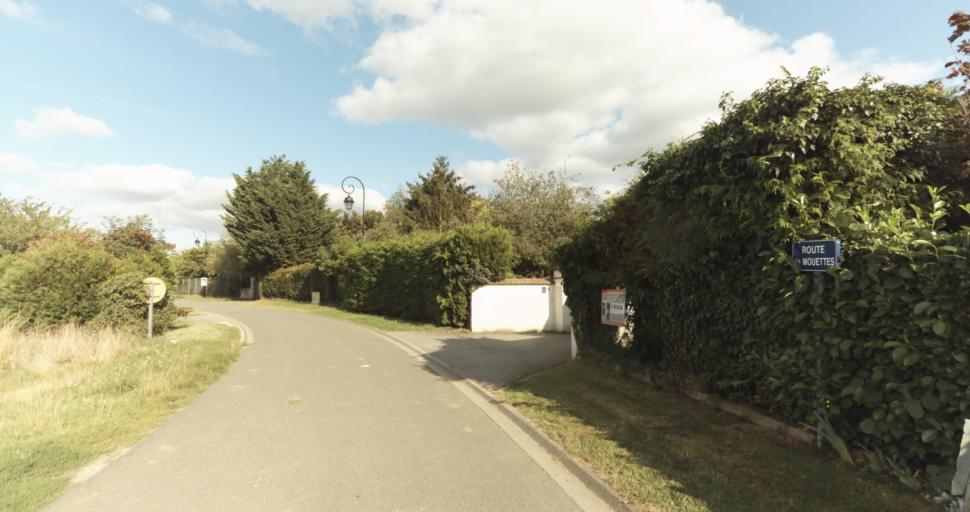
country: FR
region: Haute-Normandie
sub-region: Departement de l'Eure
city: La Couture-Boussey
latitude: 48.9033
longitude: 1.3333
